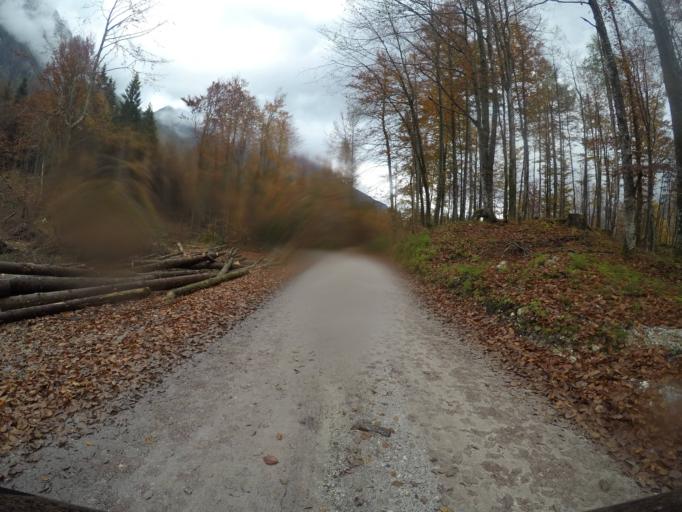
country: SI
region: Kranjska Gora
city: Mojstrana
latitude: 46.4262
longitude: 13.8683
